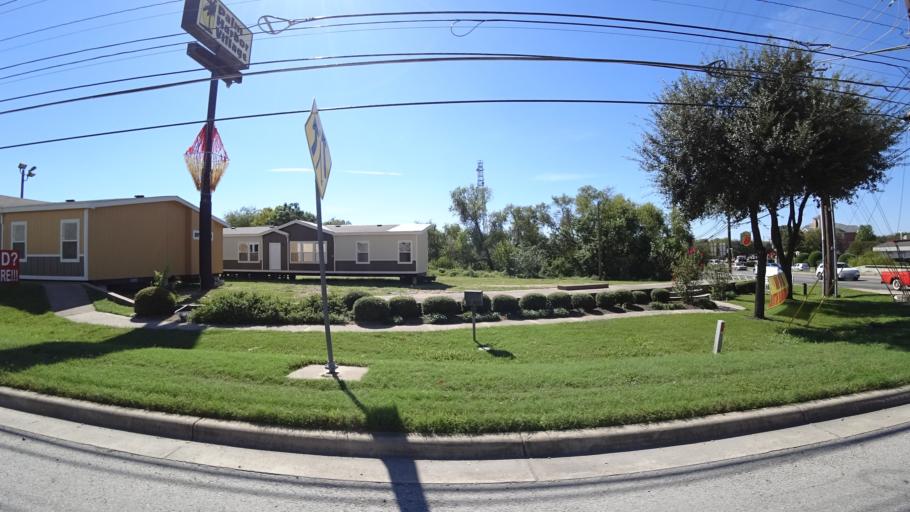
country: US
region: Texas
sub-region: Travis County
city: Austin
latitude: 30.2114
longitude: -97.7123
